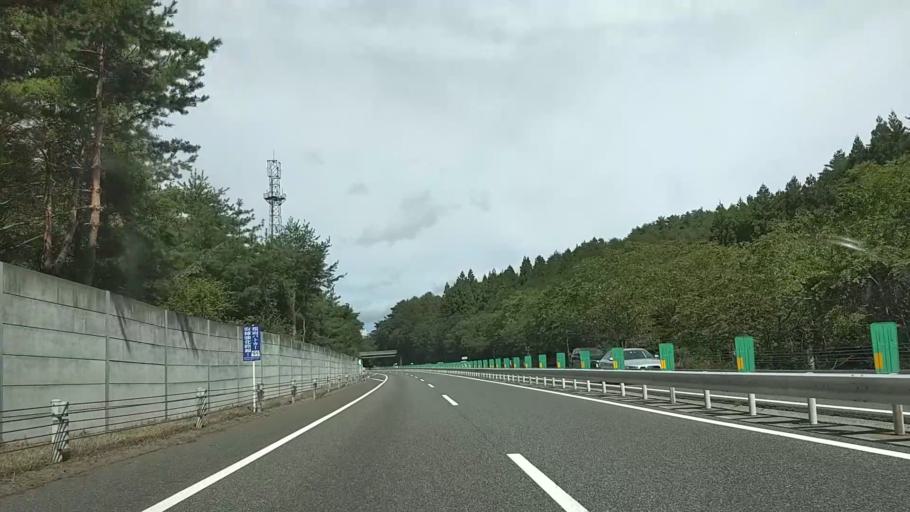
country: JP
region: Nagano
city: Chino
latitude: 35.8760
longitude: 138.3050
